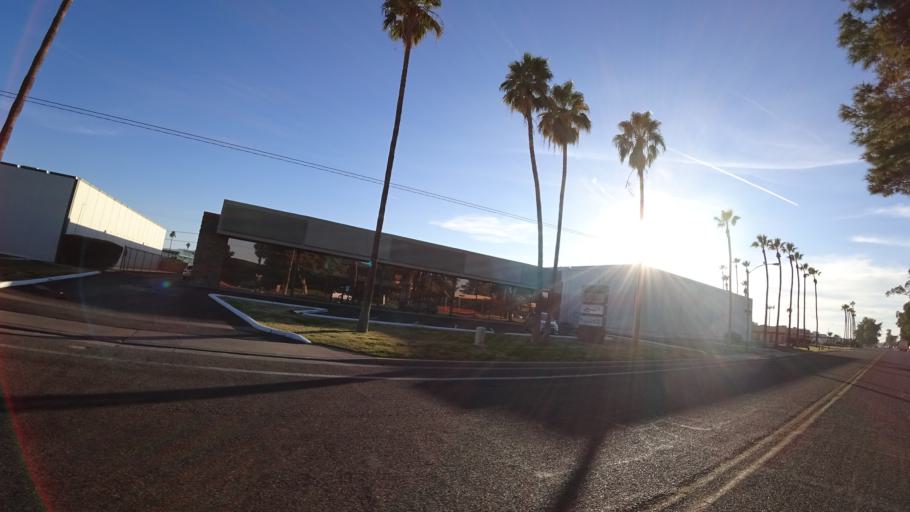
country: US
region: Arizona
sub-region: Maricopa County
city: Phoenix
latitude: 33.4241
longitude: -112.0261
